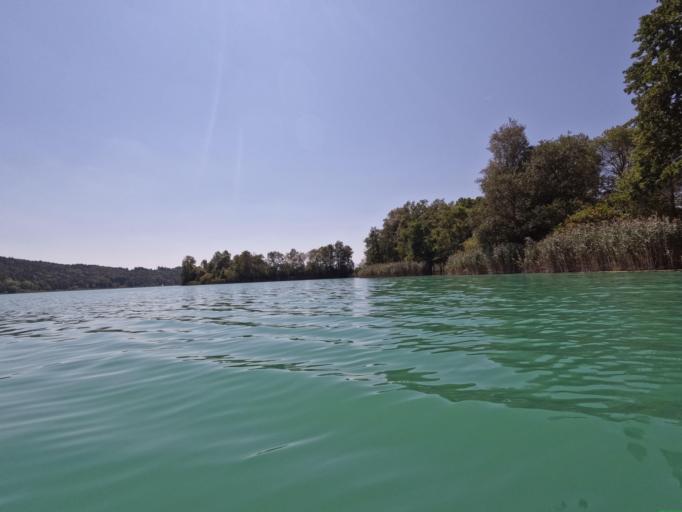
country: DE
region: Bavaria
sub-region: Upper Bavaria
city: Taching am See
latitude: 47.9794
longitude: 12.7402
